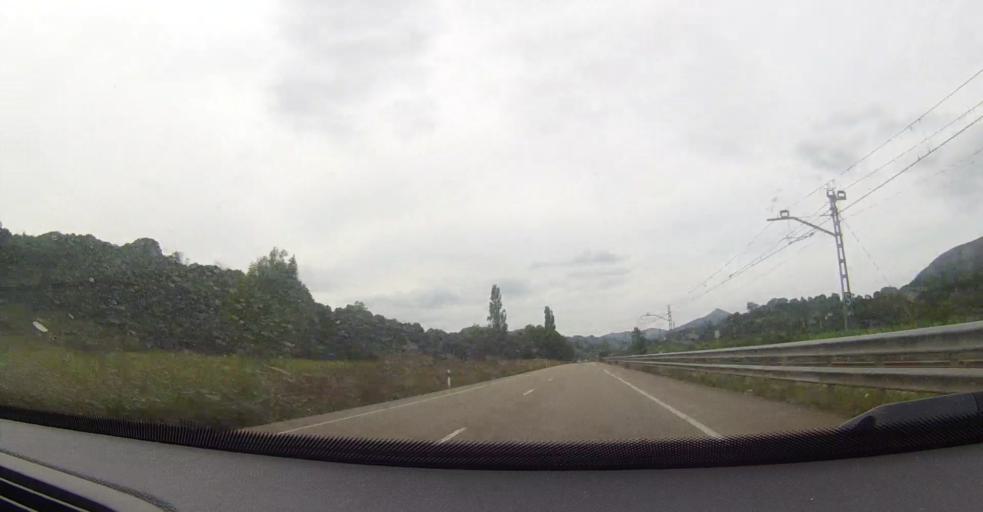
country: ES
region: Asturias
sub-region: Province of Asturias
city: Pilona
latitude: 43.3667
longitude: -5.2810
